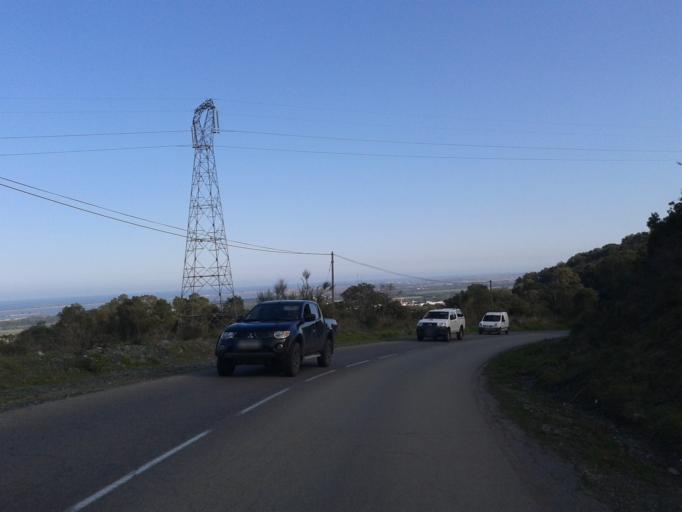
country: FR
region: Corsica
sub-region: Departement de la Haute-Corse
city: Biguglia
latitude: 42.5977
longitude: 9.4218
